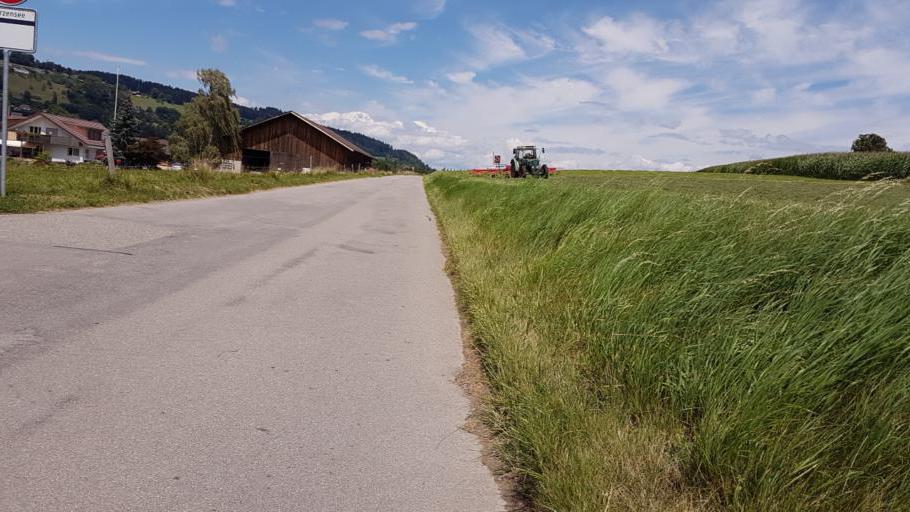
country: CH
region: Bern
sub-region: Bern-Mittelland District
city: Niederwichtrach
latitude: 46.8249
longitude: 7.5499
